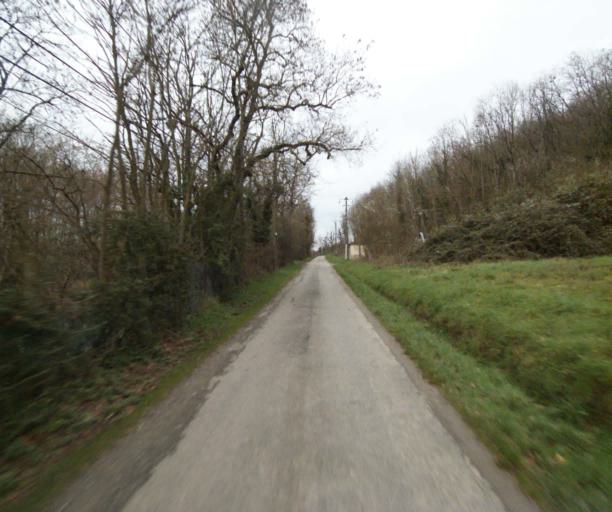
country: FR
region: Midi-Pyrenees
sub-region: Departement de l'Ariege
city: Saverdun
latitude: 43.2234
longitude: 1.5858
